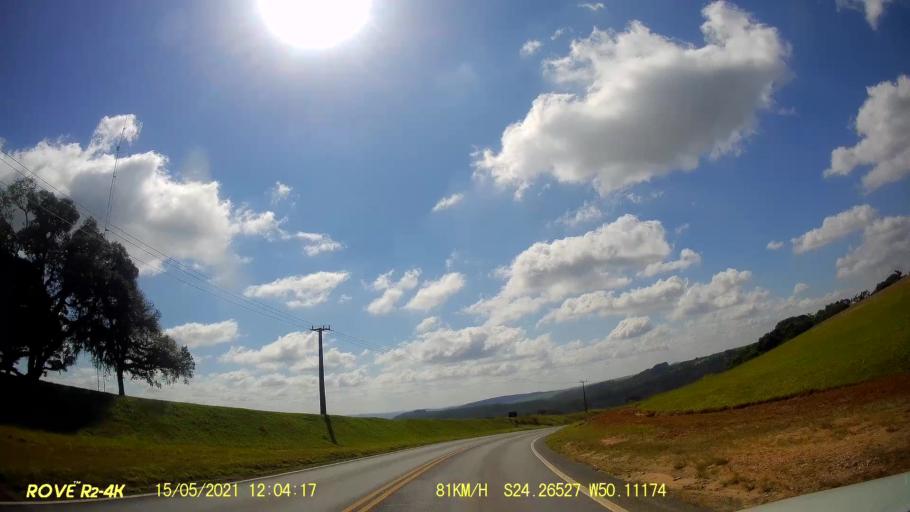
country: BR
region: Parana
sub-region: Pirai Do Sul
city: Pirai do Sul
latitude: -24.2653
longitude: -50.1118
